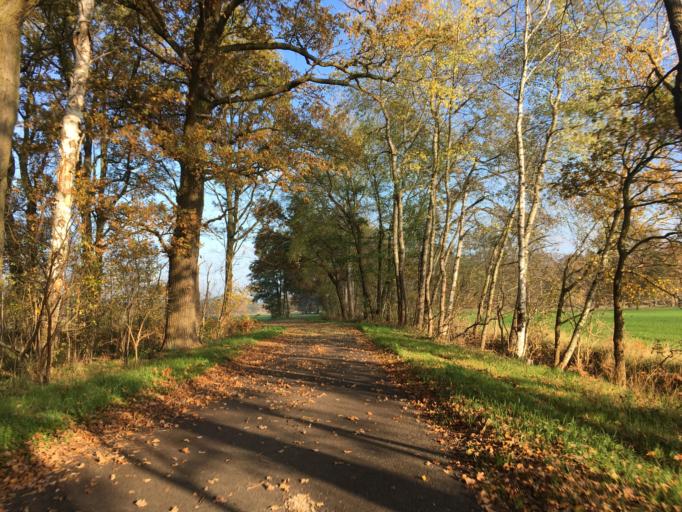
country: DE
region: Brandenburg
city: Schlepzig
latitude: 52.0434
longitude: 13.9047
